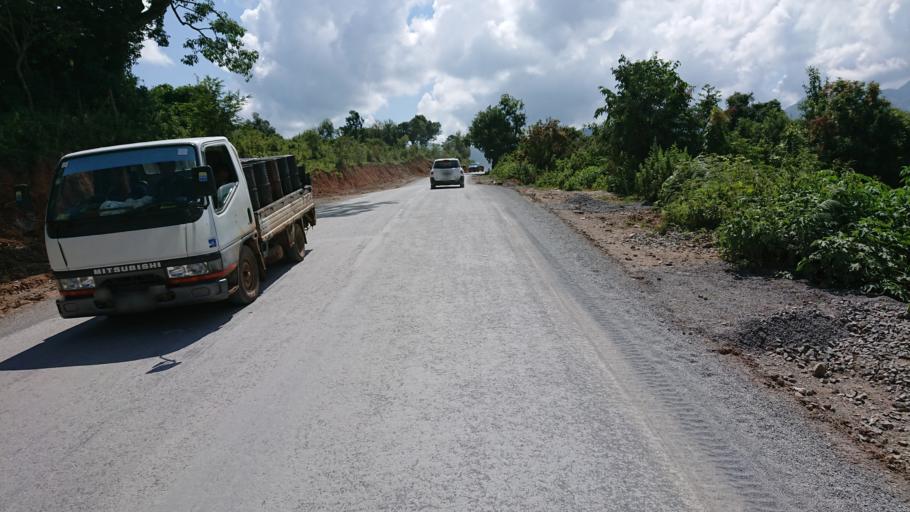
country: MM
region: Shan
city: Taunggyi
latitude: 20.8127
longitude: 97.3213
